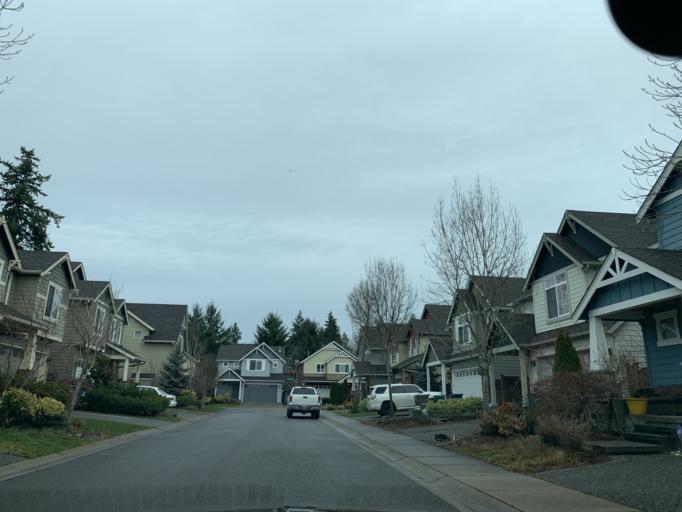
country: US
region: Washington
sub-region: King County
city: Kingsgate
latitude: 47.7445
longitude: -122.1810
